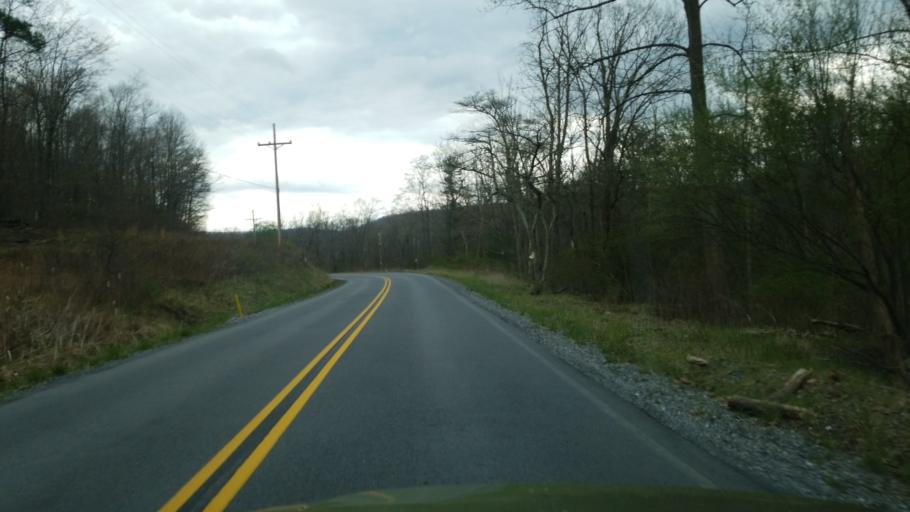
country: US
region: Pennsylvania
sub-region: Blair County
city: Tipton
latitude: 40.6487
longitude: -78.3212
